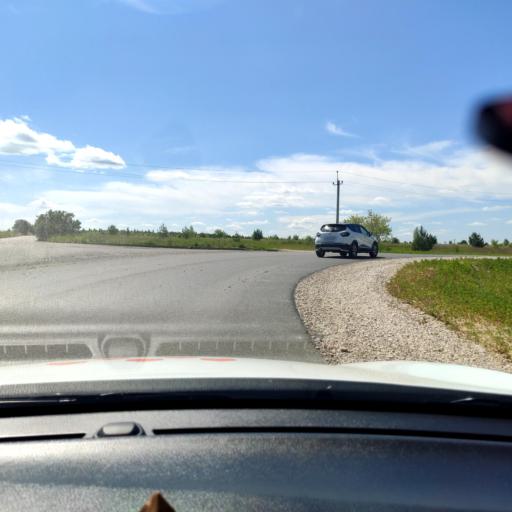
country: RU
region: Tatarstan
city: Osinovo
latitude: 55.7728
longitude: 48.8241
